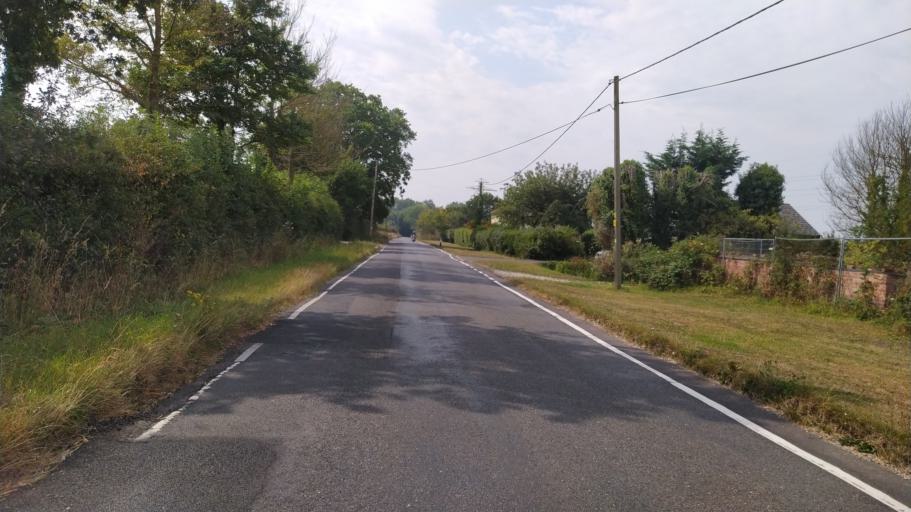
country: GB
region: England
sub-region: Hampshire
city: Romsey
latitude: 50.9890
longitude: -1.4619
